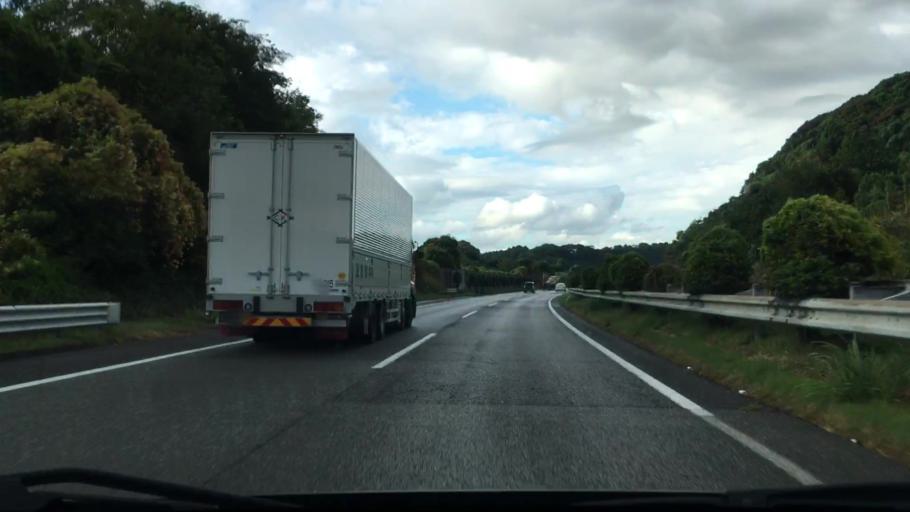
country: JP
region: Fukuoka
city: Koga
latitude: 33.7042
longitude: 130.4852
